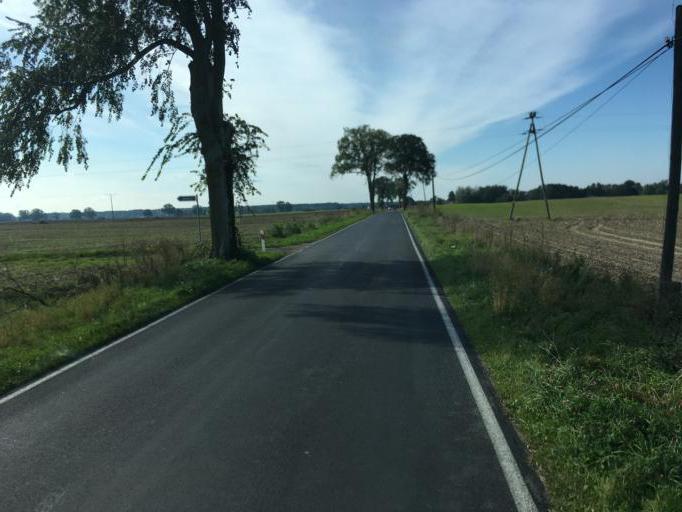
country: PL
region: Kujawsko-Pomorskie
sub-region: Powiat swiecki
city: Lniano
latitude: 53.5099
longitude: 18.1750
